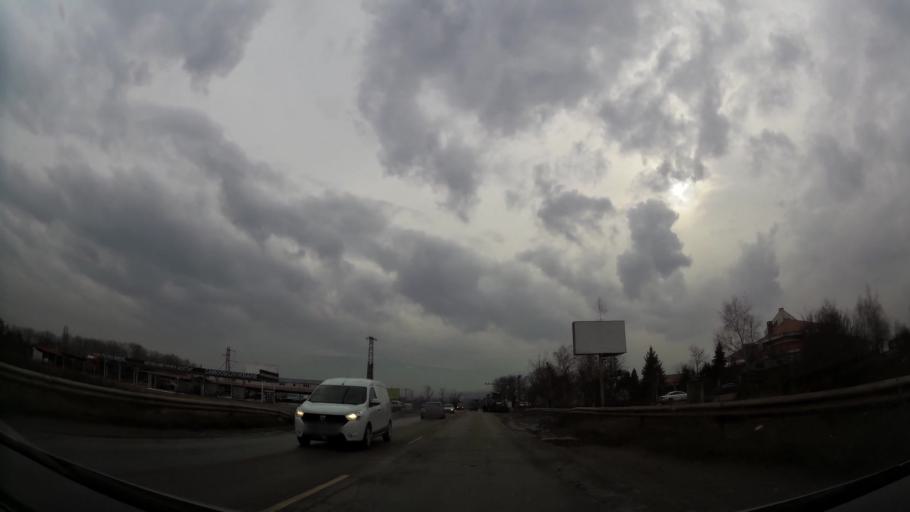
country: BG
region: Sofiya
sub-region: Obshtina Bozhurishte
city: Bozhurishte
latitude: 42.7065
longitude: 23.2303
